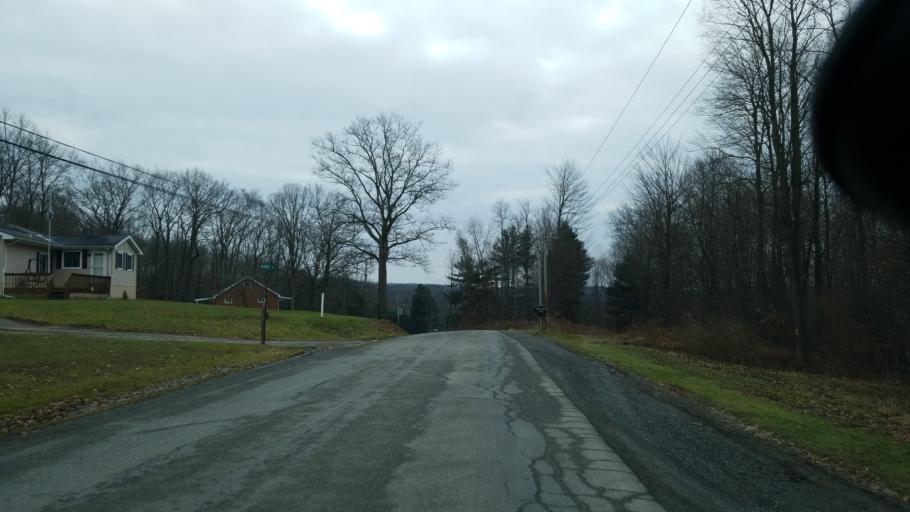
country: US
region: Pennsylvania
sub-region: Clearfield County
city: Treasure Lake
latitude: 41.1232
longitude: -78.6891
